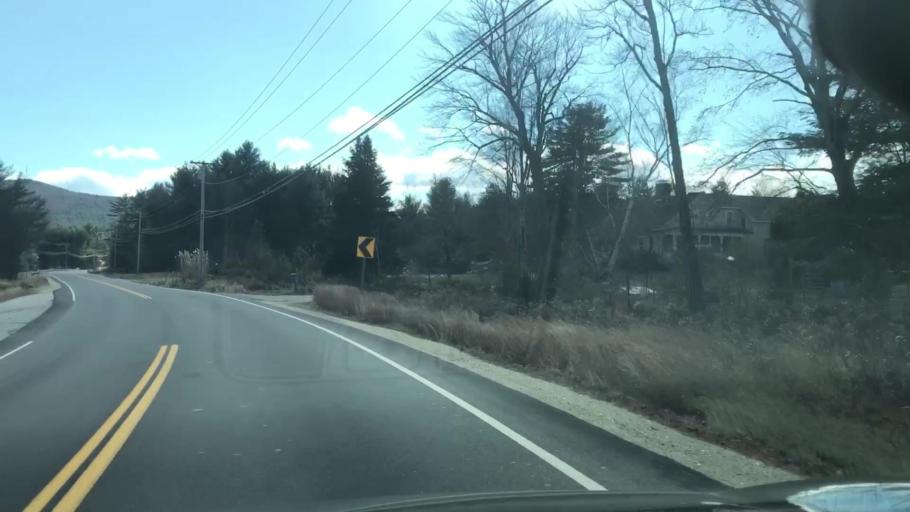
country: US
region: New Hampshire
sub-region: Strafford County
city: New Durham
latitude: 43.4276
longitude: -71.2086
